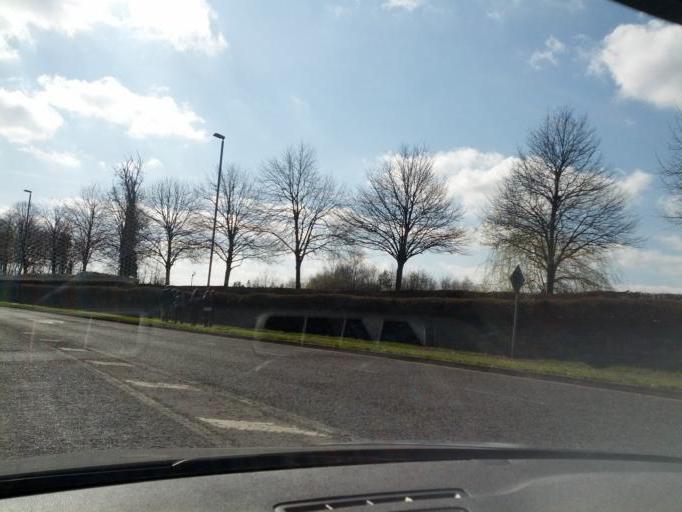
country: IE
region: Leinster
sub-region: Kildare
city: Leixlip
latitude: 53.3534
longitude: -6.5093
